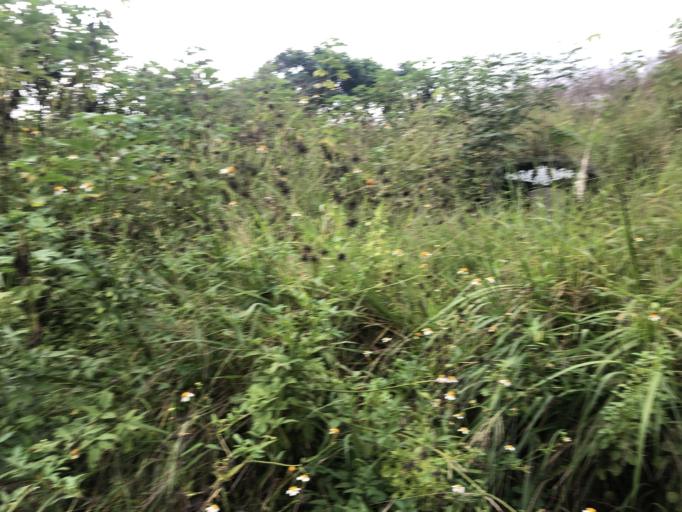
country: TW
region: Taiwan
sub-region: Tainan
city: Tainan
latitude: 22.9662
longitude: 120.1985
